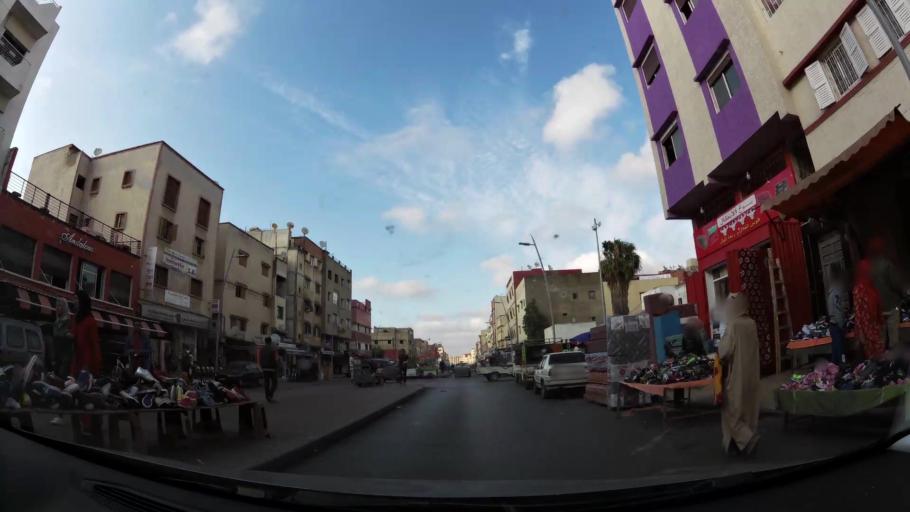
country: MA
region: Rabat-Sale-Zemmour-Zaer
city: Sale
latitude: 34.0530
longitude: -6.7811
